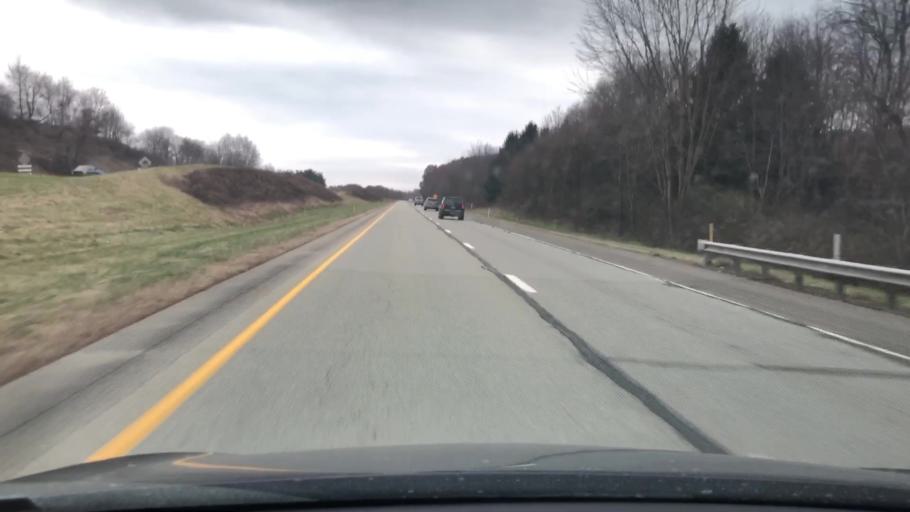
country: US
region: Pennsylvania
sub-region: Armstrong County
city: West Hills
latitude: 40.7912
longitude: -79.5763
